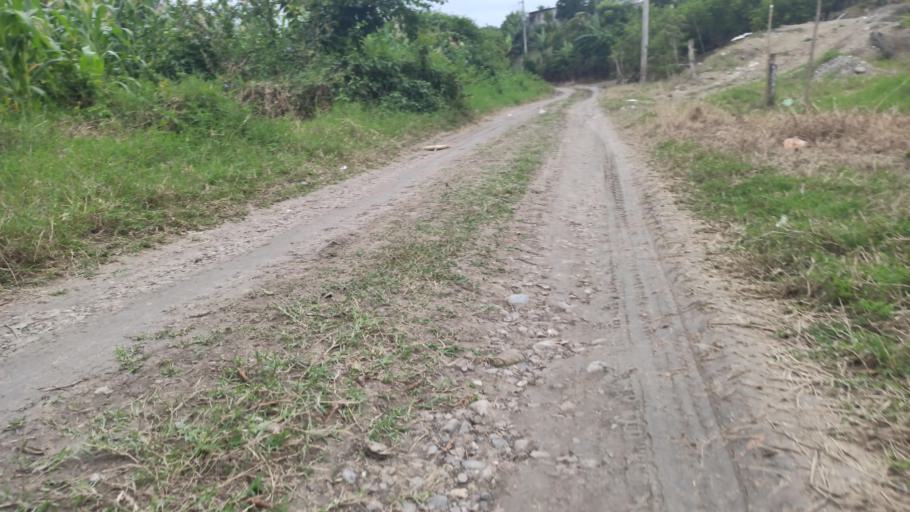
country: MX
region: Veracruz
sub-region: Papantla
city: El Chote
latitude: 20.3653
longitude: -97.4312
